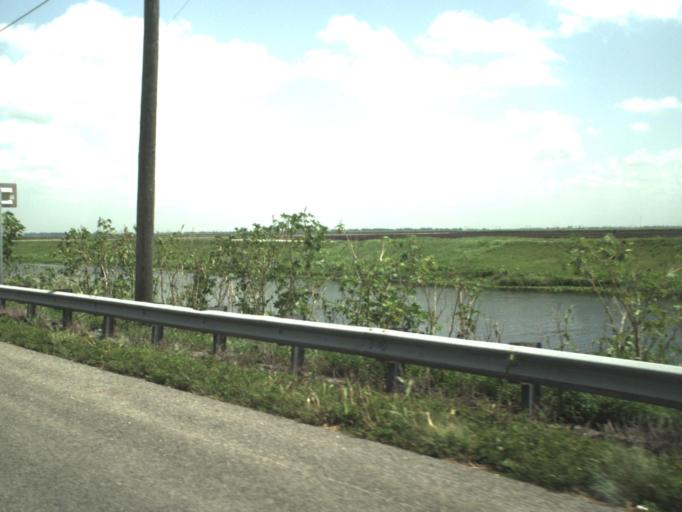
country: US
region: Florida
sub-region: Palm Beach County
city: South Bay
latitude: 26.6236
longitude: -80.7118
